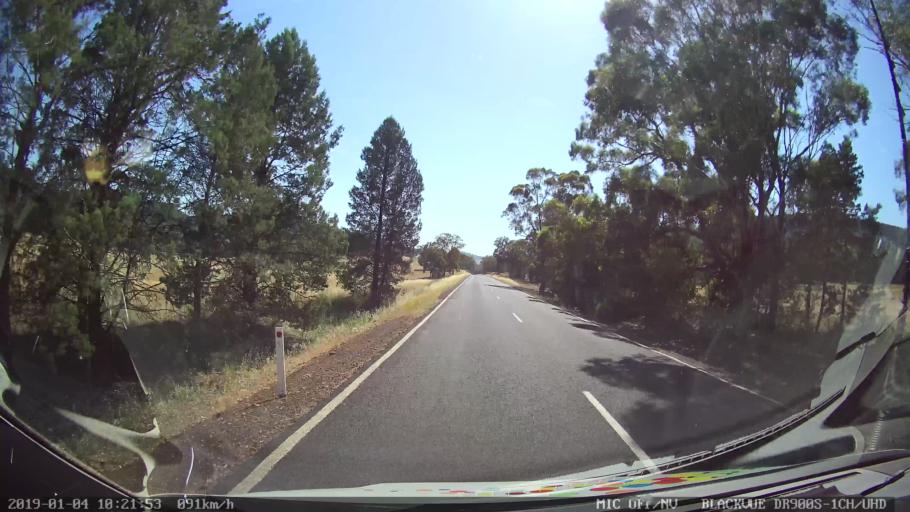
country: AU
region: New South Wales
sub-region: Cabonne
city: Canowindra
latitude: -33.3703
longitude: 148.5167
